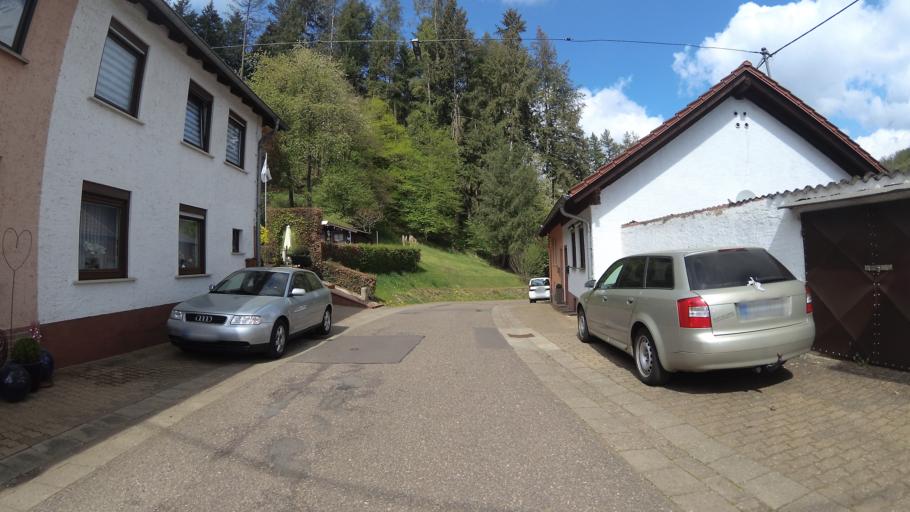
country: DE
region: Saarland
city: Schmelz
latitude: 49.4879
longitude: 6.8546
